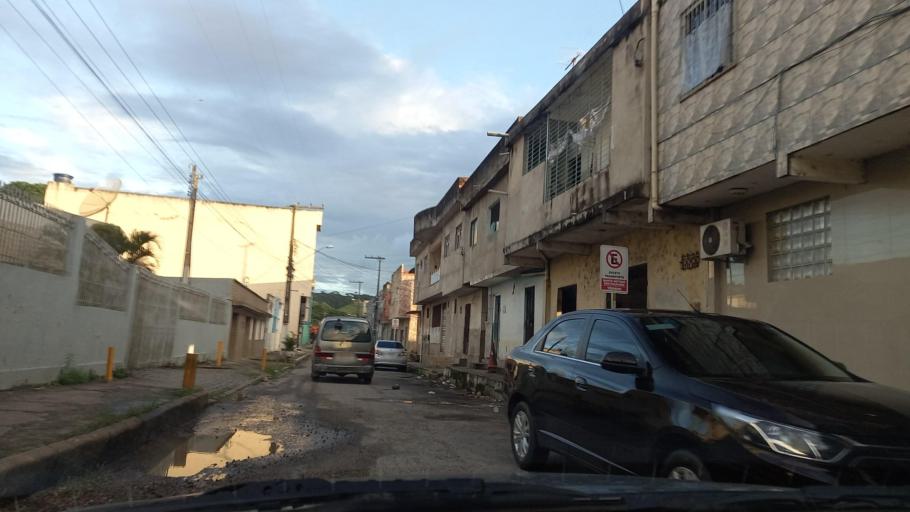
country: BR
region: Pernambuco
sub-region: Palmares
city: Palmares
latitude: -8.6868
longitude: -35.5934
